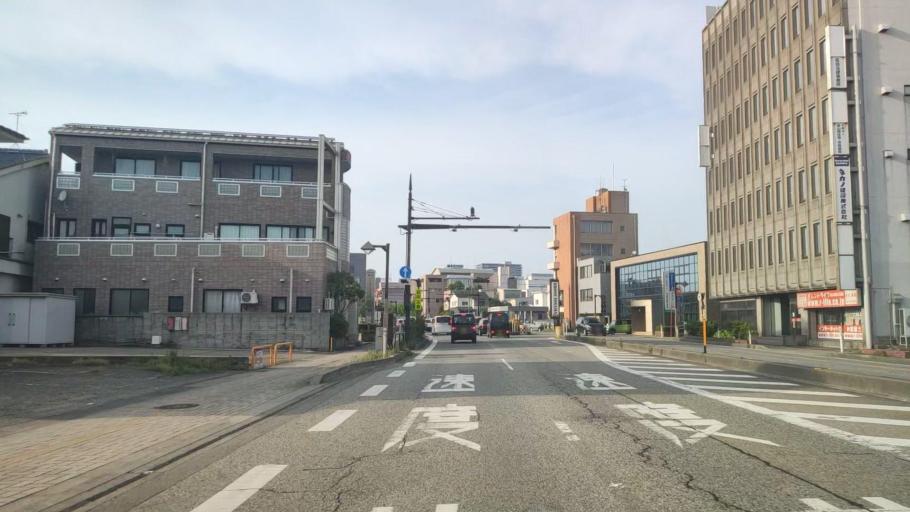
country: JP
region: Toyama
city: Toyama-shi
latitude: 36.6817
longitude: 137.2113
